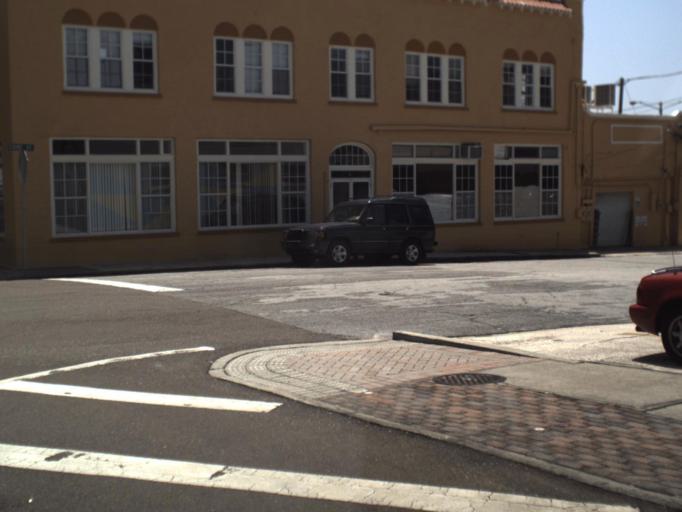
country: US
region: Florida
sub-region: Pinellas County
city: Tarpon Springs
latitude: 28.1458
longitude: -82.7567
